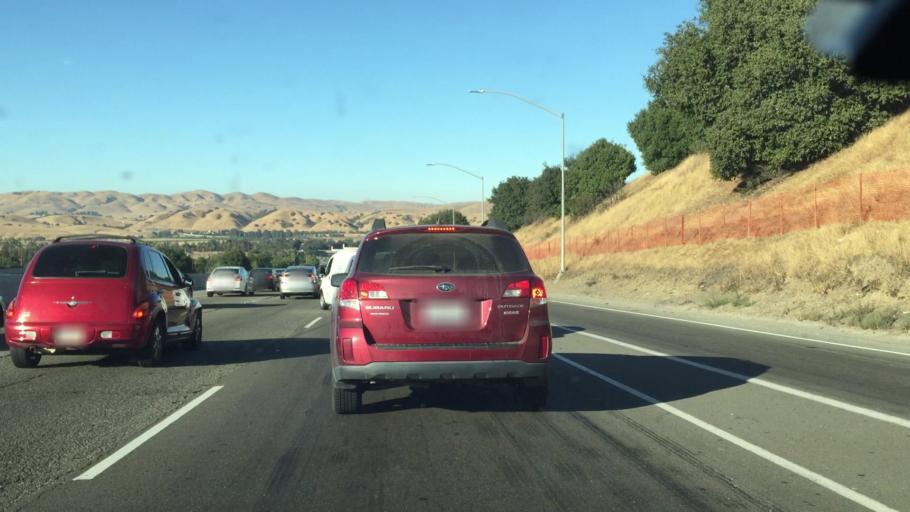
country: US
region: California
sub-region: Alameda County
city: Fremont
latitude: 37.5673
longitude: -121.8967
